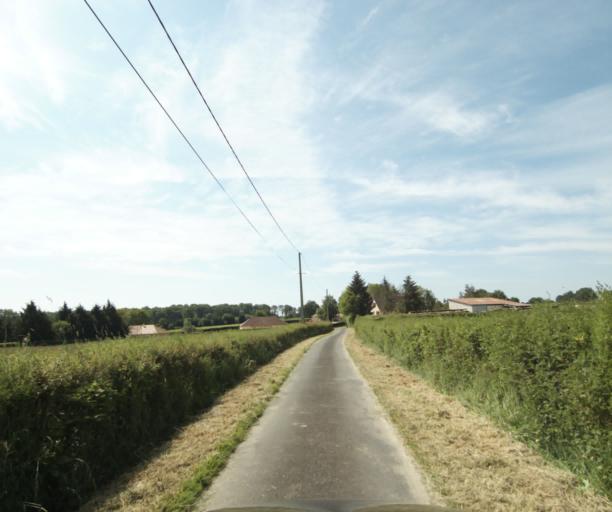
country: FR
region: Bourgogne
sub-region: Departement de Saone-et-Loire
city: Palinges
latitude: 46.5552
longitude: 4.1793
